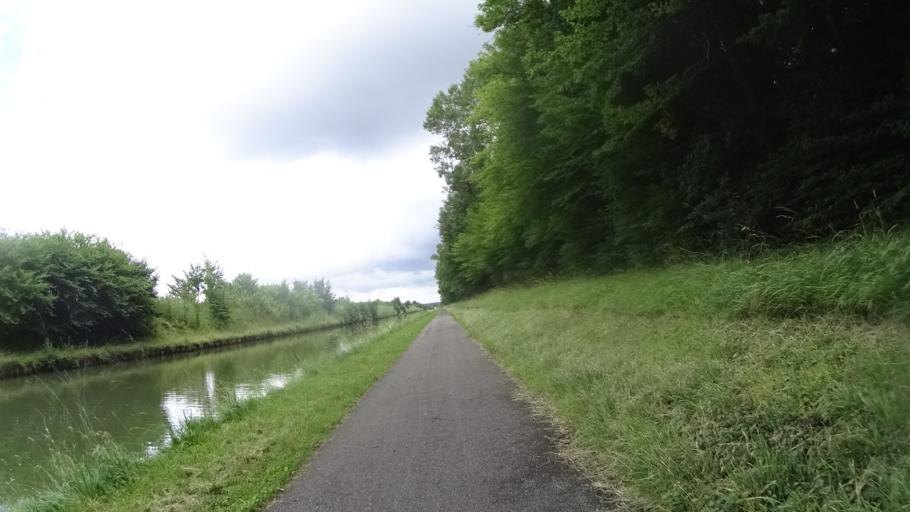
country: FR
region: Lorraine
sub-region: Departement de la Moselle
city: Lorquin
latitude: 48.7047
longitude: 6.8713
